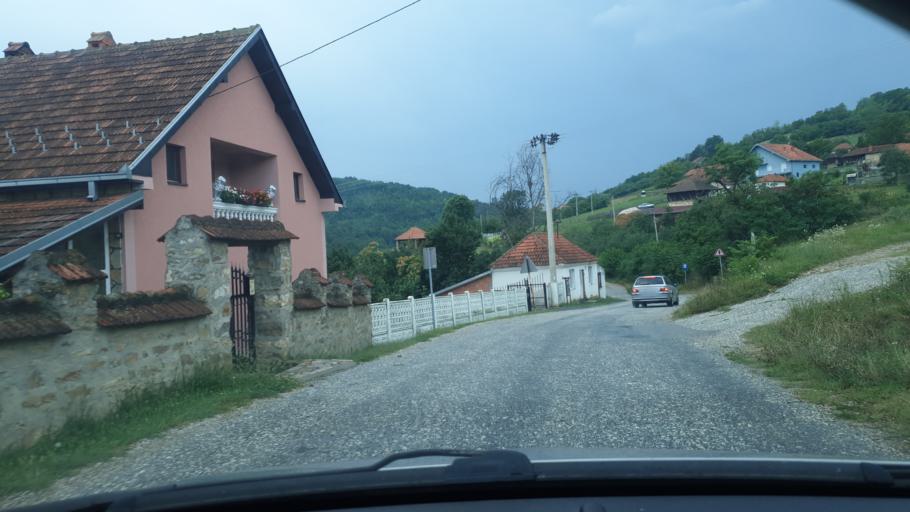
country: RS
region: Central Serbia
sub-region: Sumadijski Okrug
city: Kragujevac
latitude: 44.0723
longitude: 20.7881
